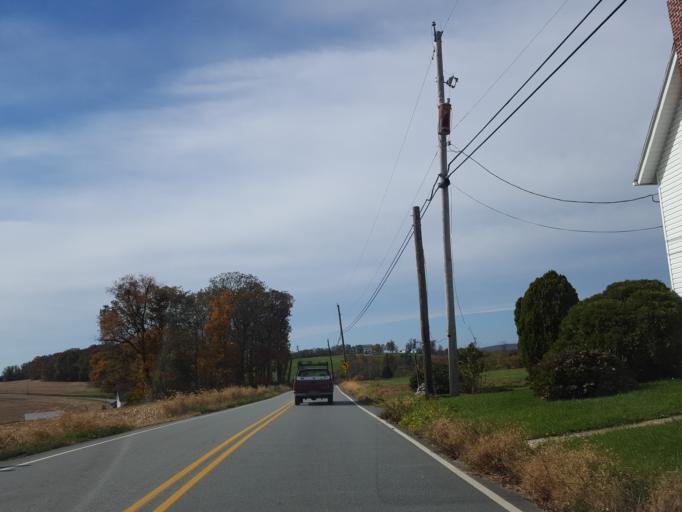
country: US
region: Pennsylvania
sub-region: York County
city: Hallam
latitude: 39.9908
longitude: -76.5624
